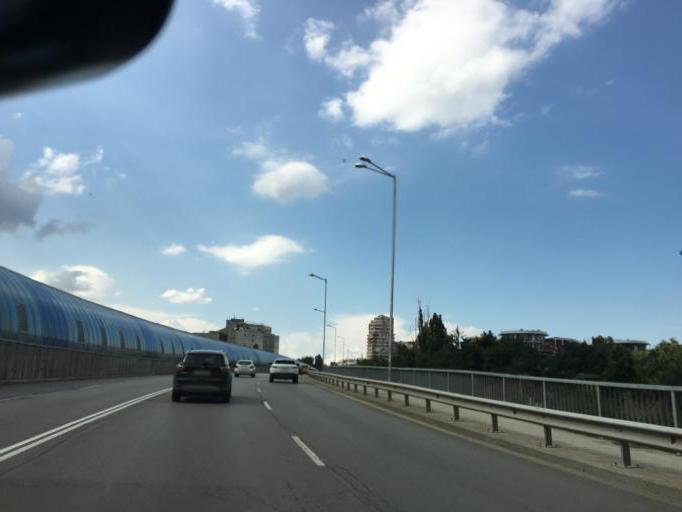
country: BG
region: Sofia-Capital
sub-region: Stolichna Obshtina
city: Sofia
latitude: 42.6666
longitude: 23.3539
